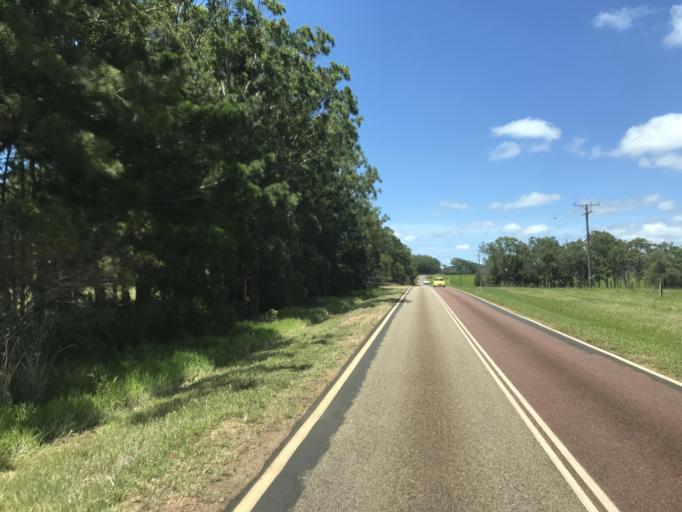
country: AU
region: Queensland
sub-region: Tablelands
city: Ravenshoe
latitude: -17.5202
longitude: 145.4519
